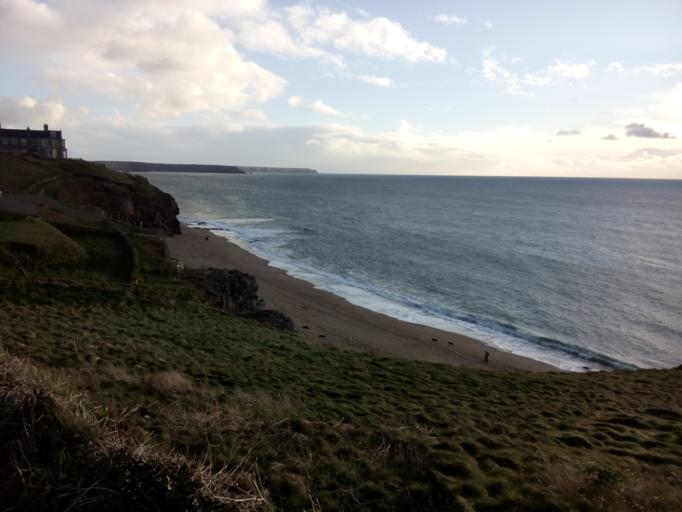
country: GB
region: England
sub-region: Cornwall
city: Porthleven
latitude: 50.0797
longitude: -5.3100
